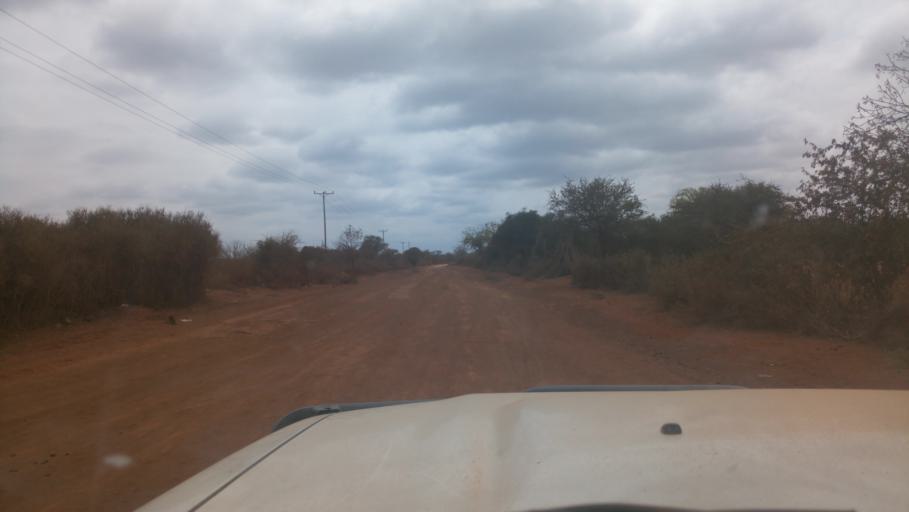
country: KE
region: Makueni
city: Wote
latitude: -1.8301
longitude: 37.9318
